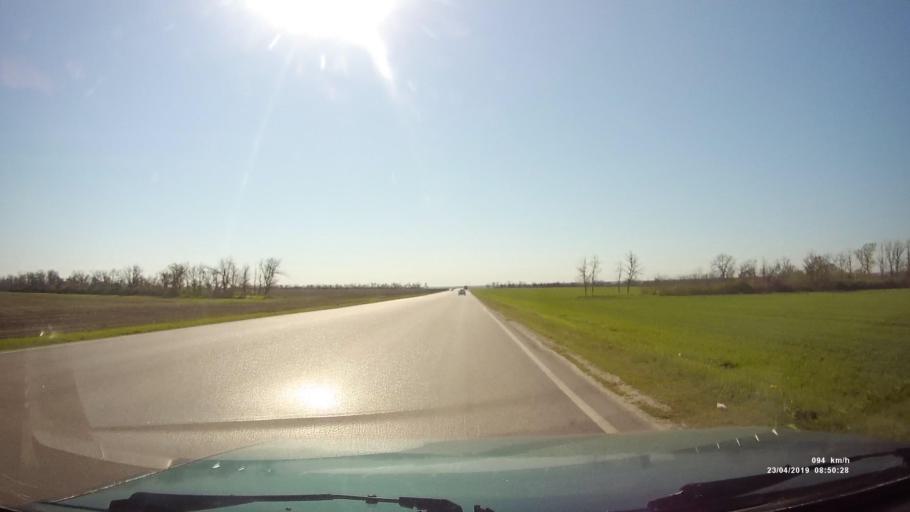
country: RU
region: Rostov
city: Gigant
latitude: 46.4966
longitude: 41.4280
